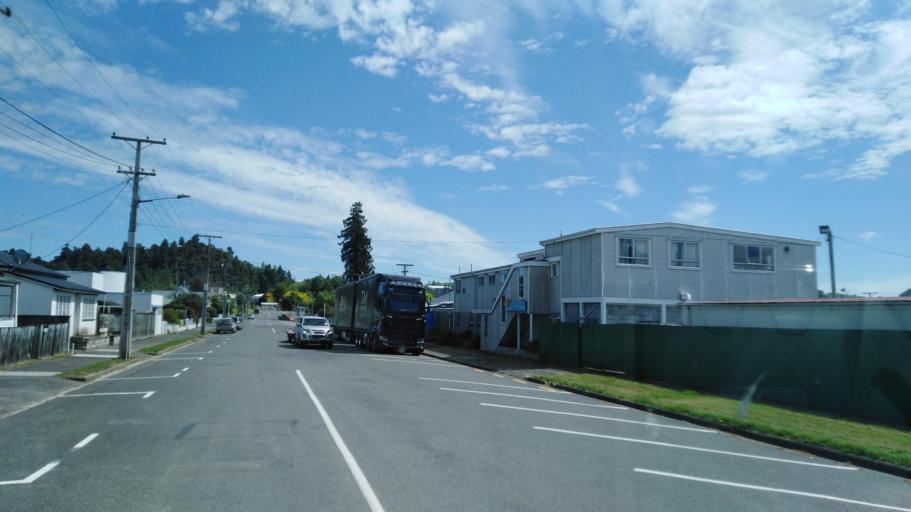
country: NZ
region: Manawatu-Wanganui
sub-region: Ruapehu District
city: Waiouru
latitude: -39.6787
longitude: 175.8021
